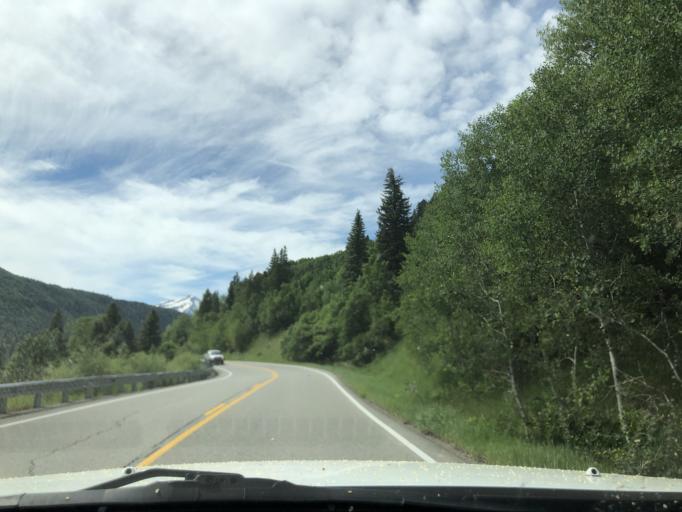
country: US
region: Colorado
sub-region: Delta County
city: Paonia
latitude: 38.9785
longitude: -107.3444
